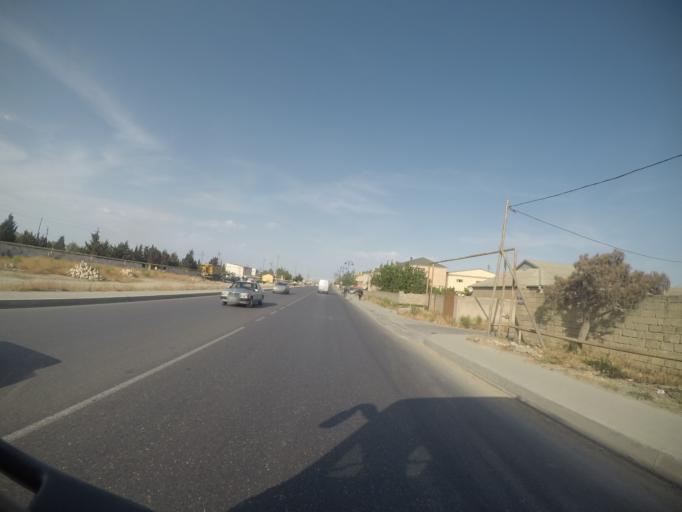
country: AZ
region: Baki
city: Bilajari
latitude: 40.4432
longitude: 49.7884
